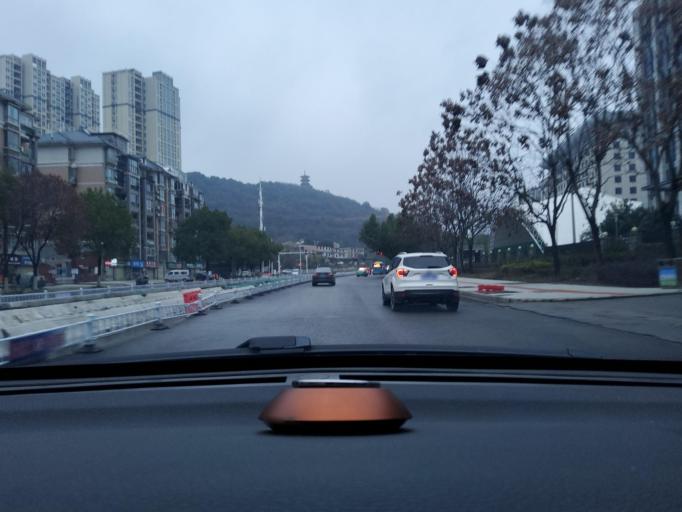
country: CN
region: Hubei
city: Tuanchengshan
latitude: 30.1952
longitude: 115.0177
